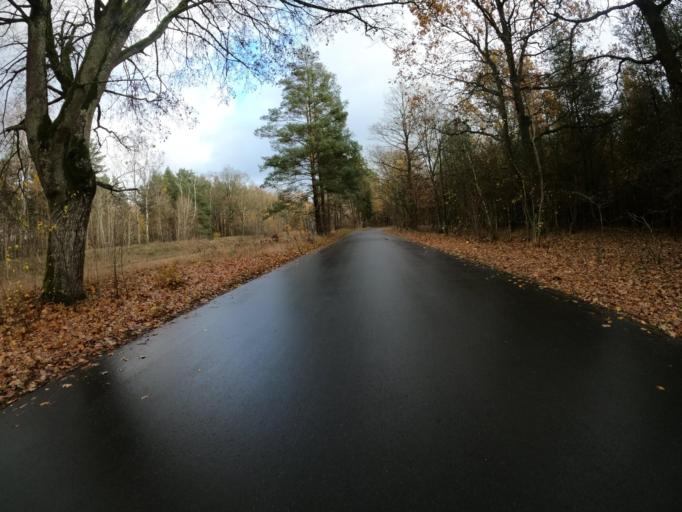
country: PL
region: West Pomeranian Voivodeship
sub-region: Powiat walecki
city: Tuczno
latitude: 53.2310
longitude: 16.2639
